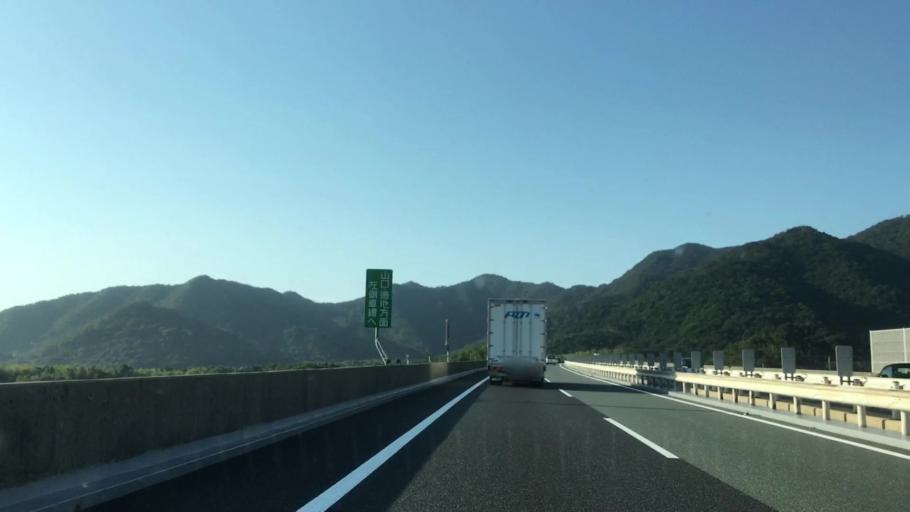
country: JP
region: Yamaguchi
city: Ogori-shimogo
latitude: 34.0936
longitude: 131.4555
